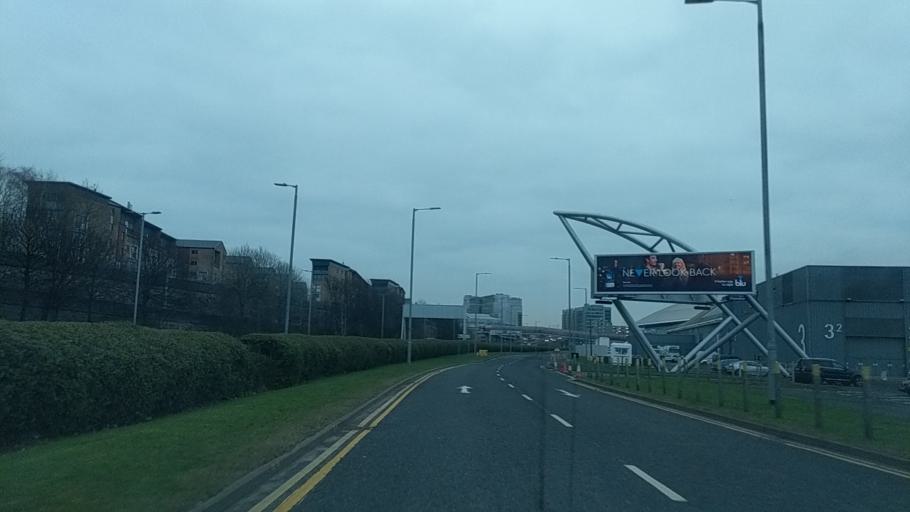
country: GB
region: Scotland
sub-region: Glasgow City
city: Glasgow
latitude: 55.8627
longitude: -4.2922
